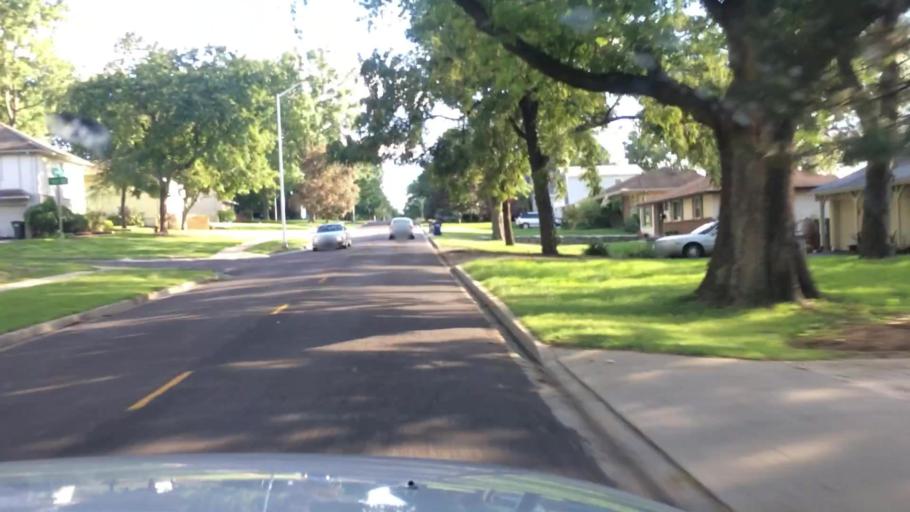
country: US
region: Kansas
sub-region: Johnson County
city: Overland Park
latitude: 38.9754
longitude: -94.6581
